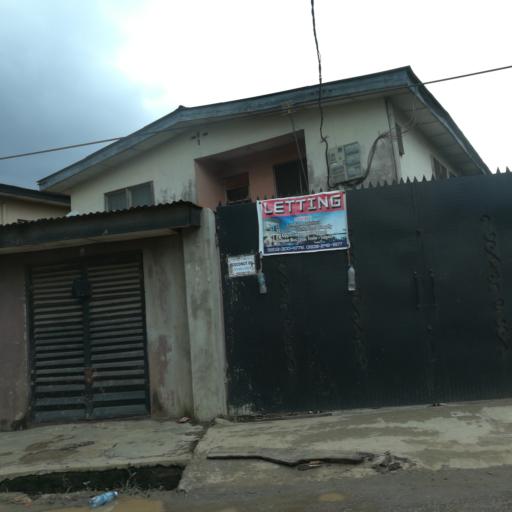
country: NG
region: Lagos
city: Agege
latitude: 6.6085
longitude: 3.3014
